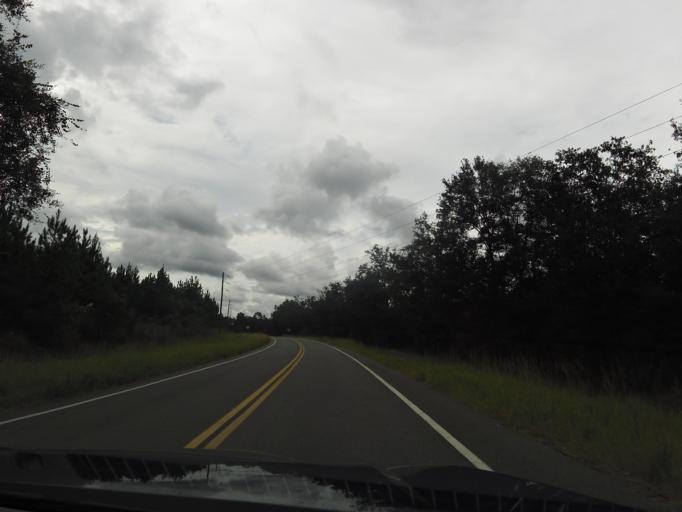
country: US
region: Florida
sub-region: Baker County
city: Macclenny
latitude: 30.4433
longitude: -82.1983
